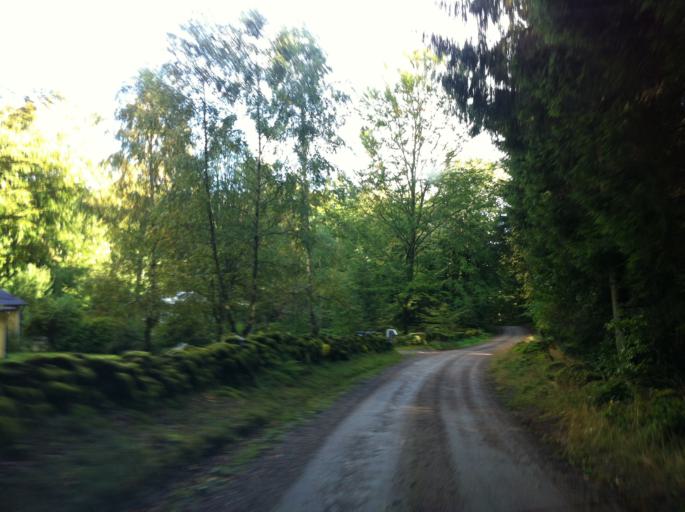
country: SE
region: Skane
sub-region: Hassleholms Kommun
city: Sosdala
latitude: 56.1300
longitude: 13.5835
